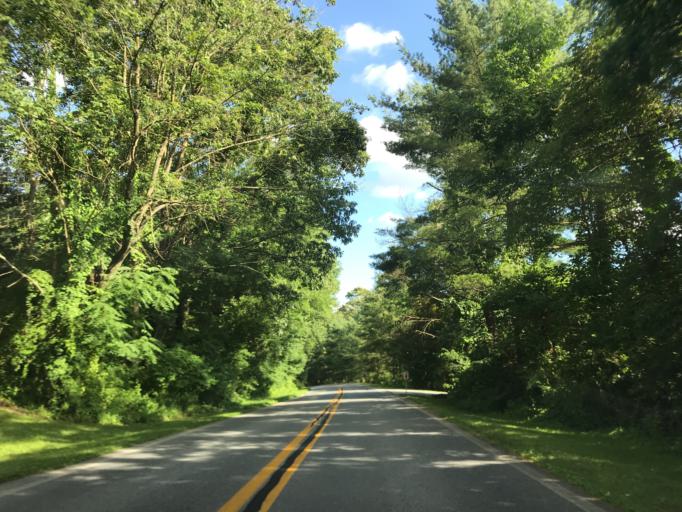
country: US
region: Maryland
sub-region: Carroll County
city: Hampstead
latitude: 39.6595
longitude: -76.8139
